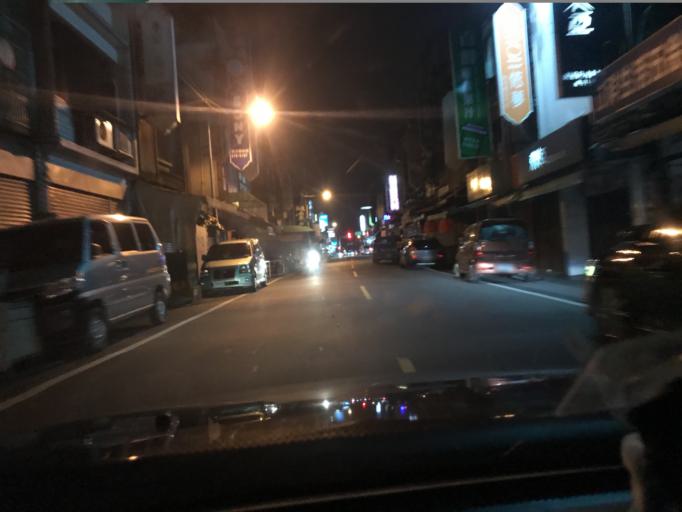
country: TW
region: Taiwan
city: Daxi
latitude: 24.8652
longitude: 121.2153
